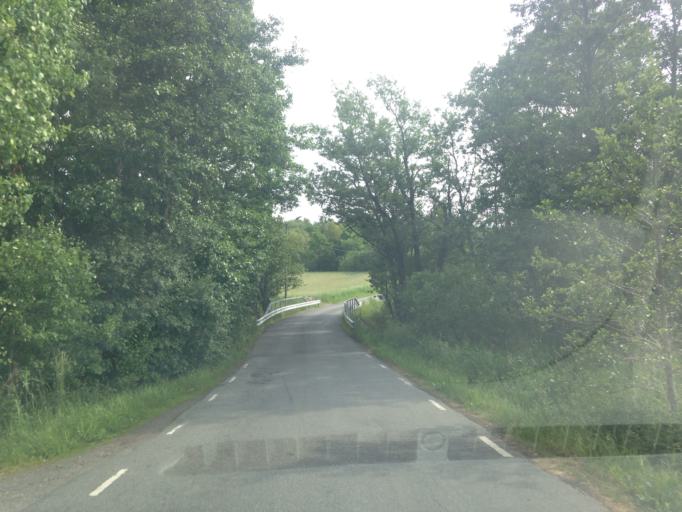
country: SE
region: Vaestra Goetaland
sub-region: Goteborg
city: Majorna
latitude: 57.7536
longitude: 11.8676
